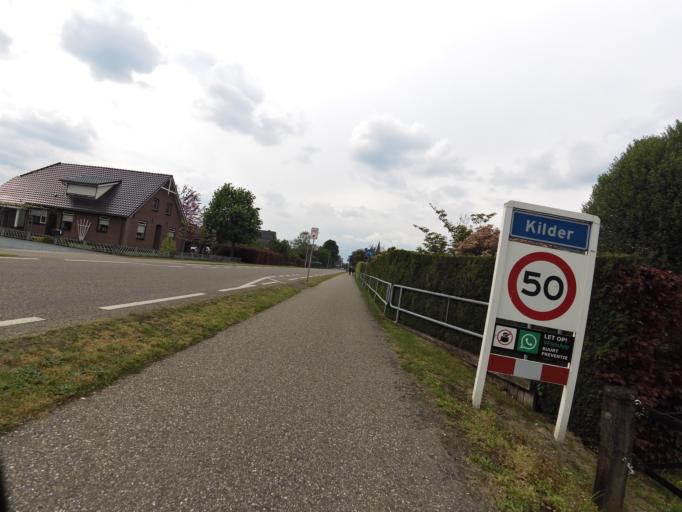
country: NL
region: Gelderland
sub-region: Gemeente Doetinchem
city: Doetinchem
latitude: 51.9345
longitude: 6.2355
